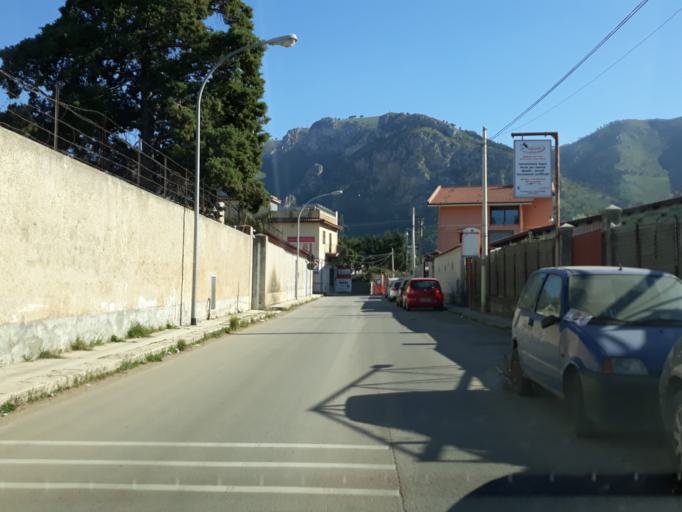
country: IT
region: Sicily
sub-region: Palermo
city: Villa Ciambra
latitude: 38.0849
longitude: 13.3450
